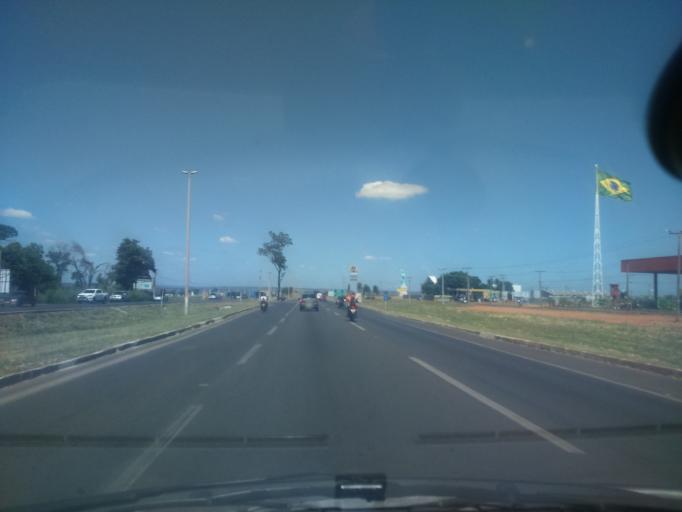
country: BR
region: Goias
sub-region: Luziania
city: Luziania
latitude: -16.0925
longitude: -47.9827
